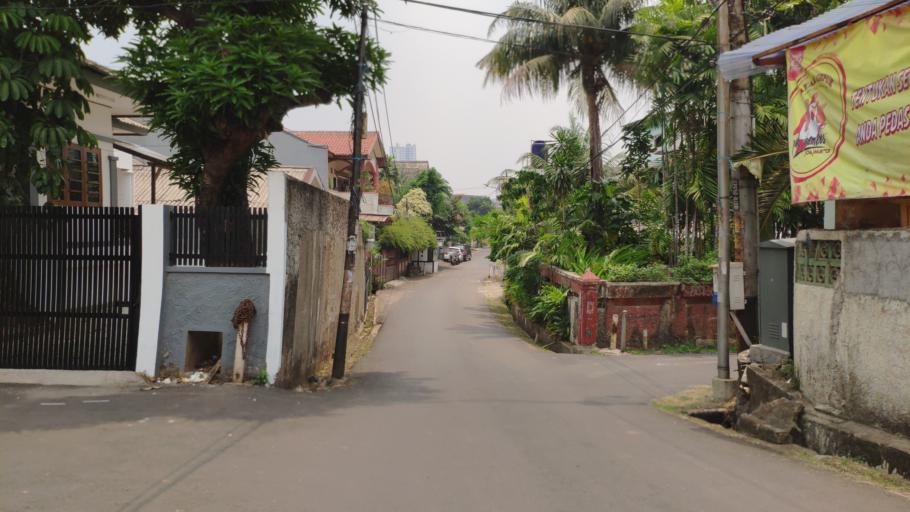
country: ID
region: Banten
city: South Tangerang
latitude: -6.2602
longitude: 106.7707
